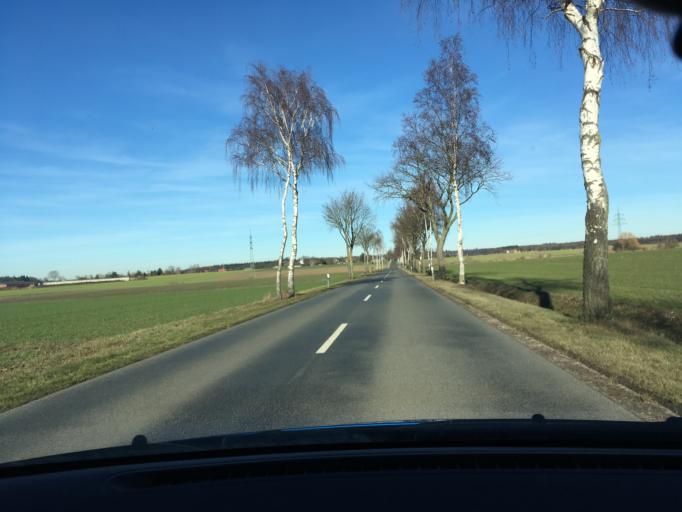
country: DE
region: Lower Saxony
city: Schwienau
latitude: 52.9946
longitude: 10.4425
